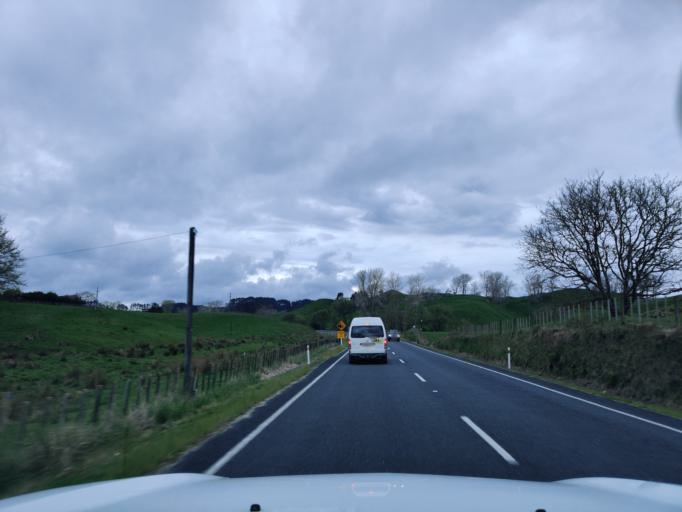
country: NZ
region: Waikato
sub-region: Otorohanga District
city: Otorohanga
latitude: -38.4514
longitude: 175.1635
